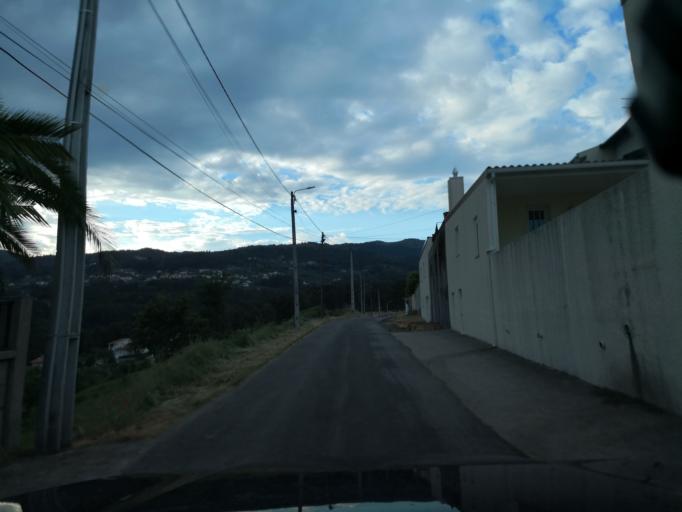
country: PT
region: Vila Real
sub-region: Vila Real
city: Vila Real
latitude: 41.3091
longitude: -7.7689
